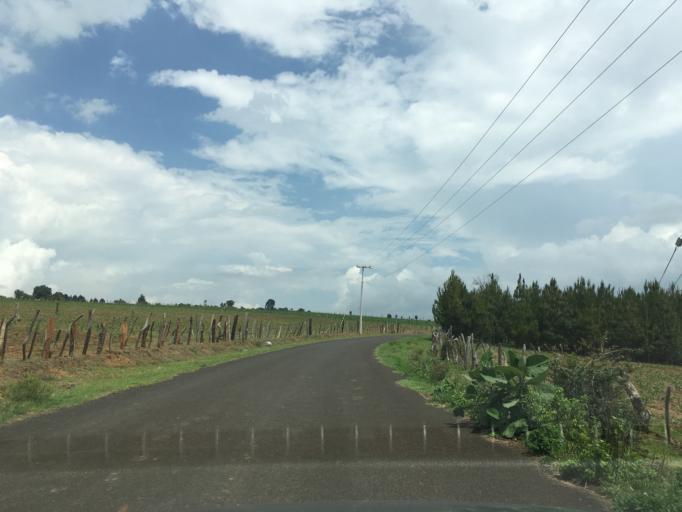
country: MX
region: Michoacan
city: Acuitzio del Canje
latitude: 19.5171
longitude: -101.2499
